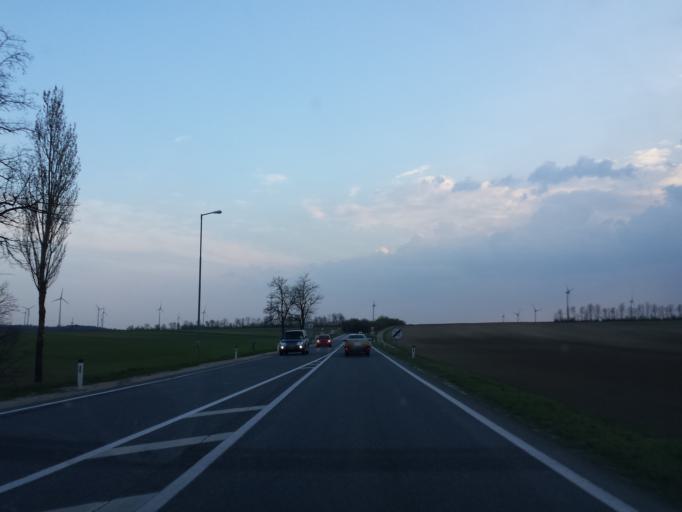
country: AT
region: Lower Austria
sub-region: Politischer Bezirk Mistelbach
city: Wilfersdorf
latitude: 48.5612
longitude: 16.6365
